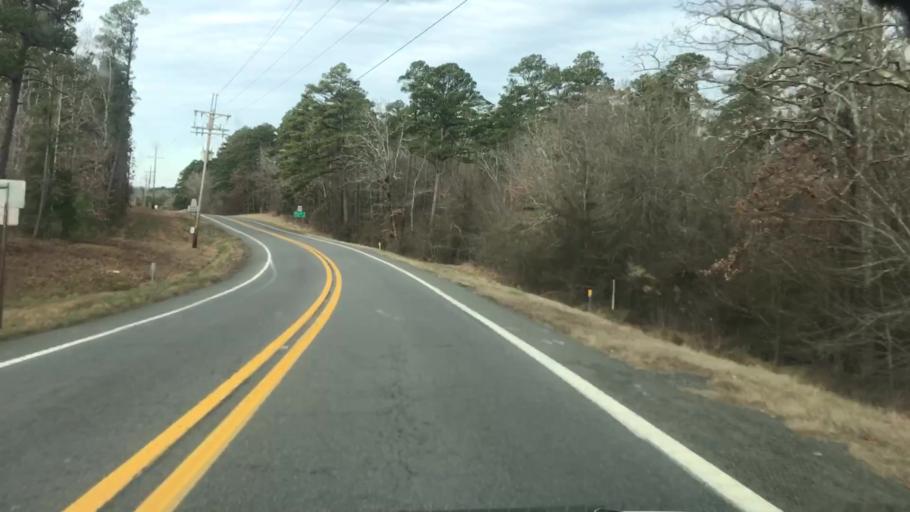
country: US
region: Arkansas
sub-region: Montgomery County
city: Mount Ida
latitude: 34.6087
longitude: -93.6746
